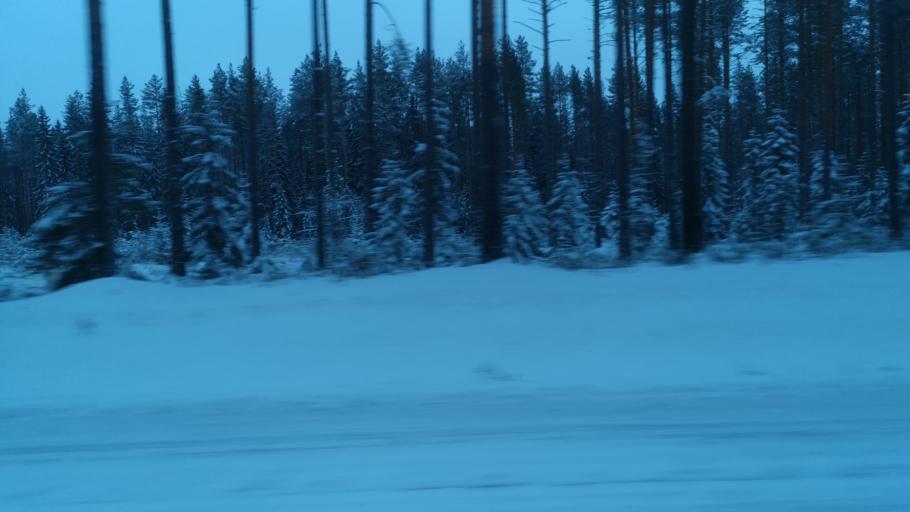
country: FI
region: Southern Savonia
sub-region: Savonlinna
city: Savonlinna
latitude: 61.9685
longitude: 28.8169
